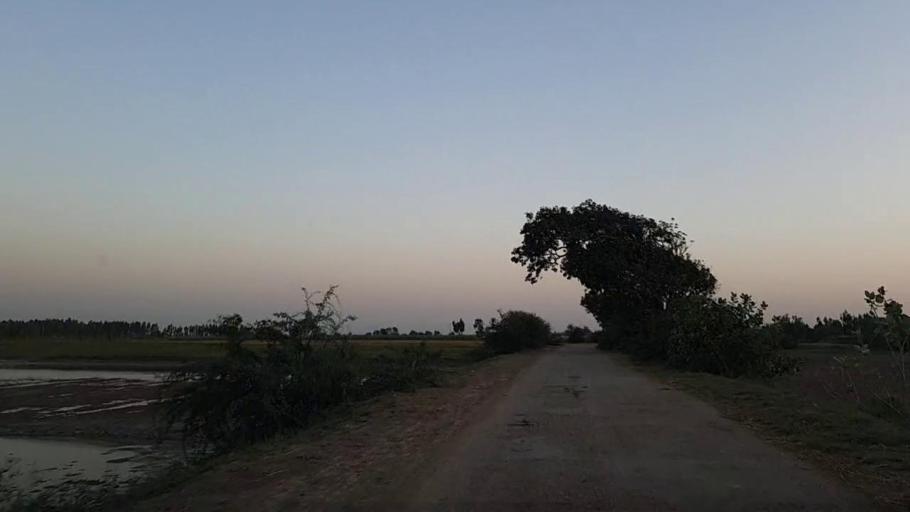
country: PK
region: Sindh
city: Mirpur Batoro
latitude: 24.6161
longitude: 68.1845
